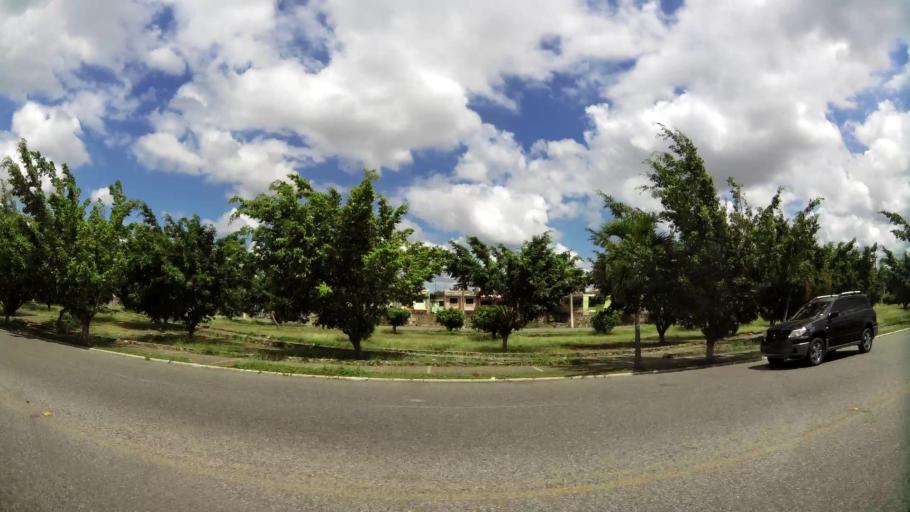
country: DO
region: Santo Domingo
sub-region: Santo Domingo
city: Santo Domingo Este
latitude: 18.4799
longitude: -69.8650
